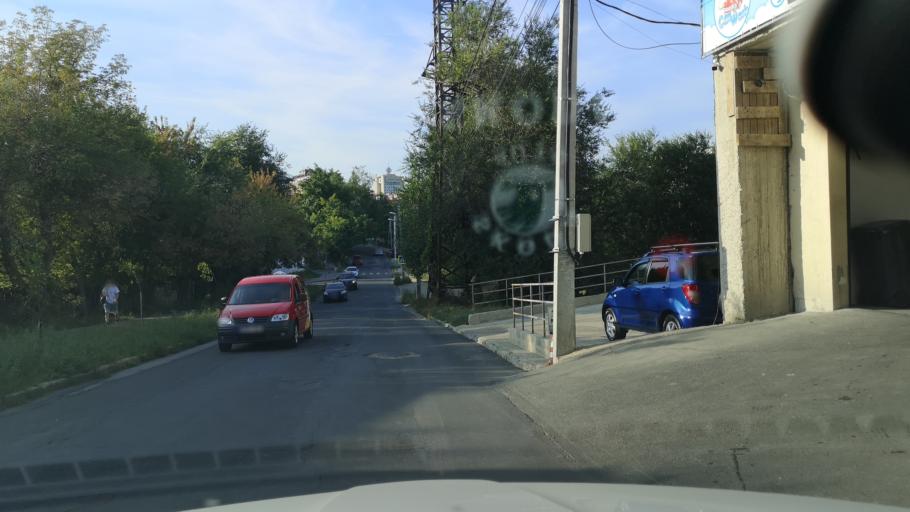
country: MD
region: Chisinau
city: Chisinau
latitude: 47.0096
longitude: 28.8482
